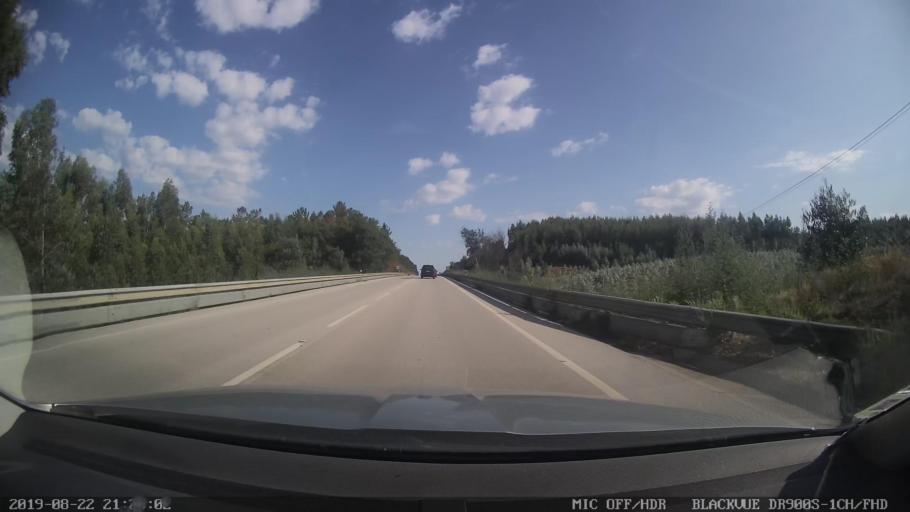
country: PT
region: Leiria
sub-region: Pedrogao Grande
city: Pedrogao Grande
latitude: 39.8872
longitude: -8.1206
